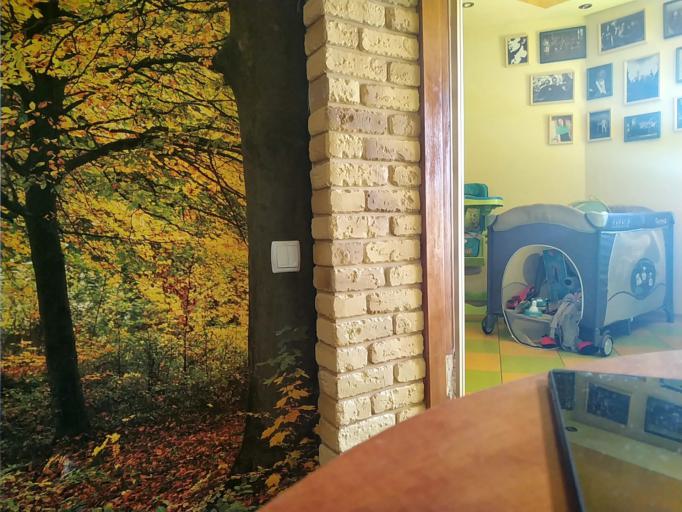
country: RU
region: Tverskaya
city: Vydropuzhsk
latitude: 57.4442
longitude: 34.7376
